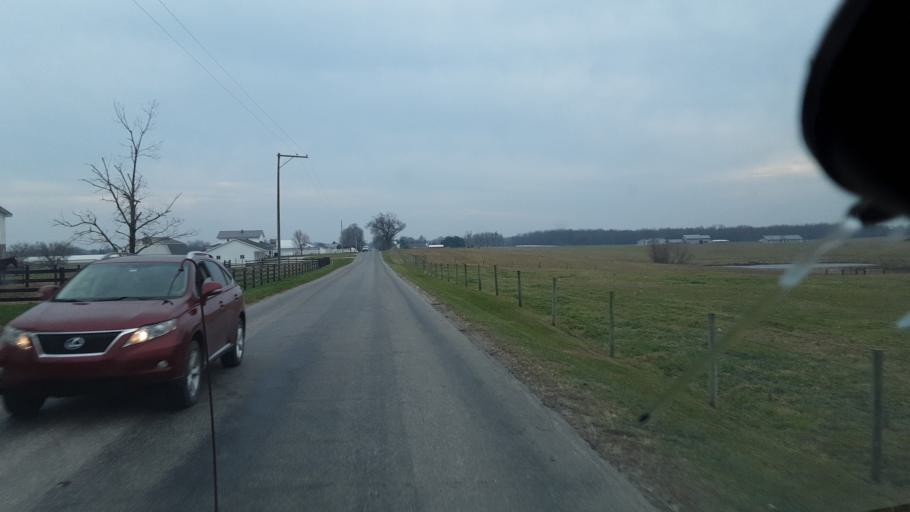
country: US
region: Indiana
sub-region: Elkhart County
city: Middlebury
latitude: 41.7030
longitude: -85.6202
